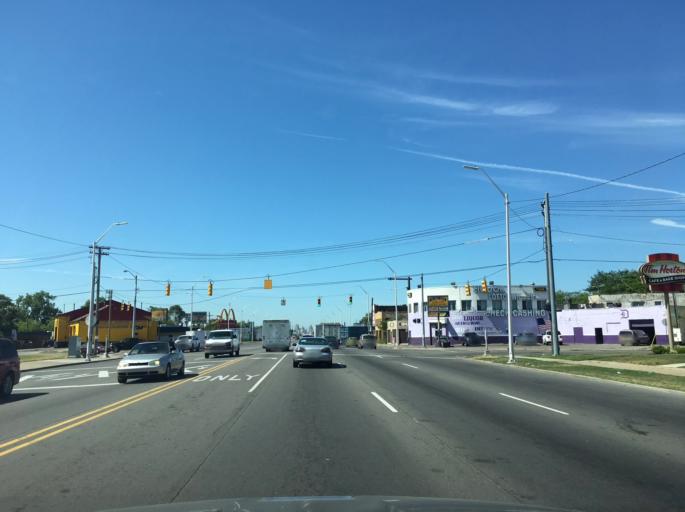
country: US
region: Michigan
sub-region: Wayne County
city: Hamtramck
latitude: 42.4009
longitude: -83.0002
